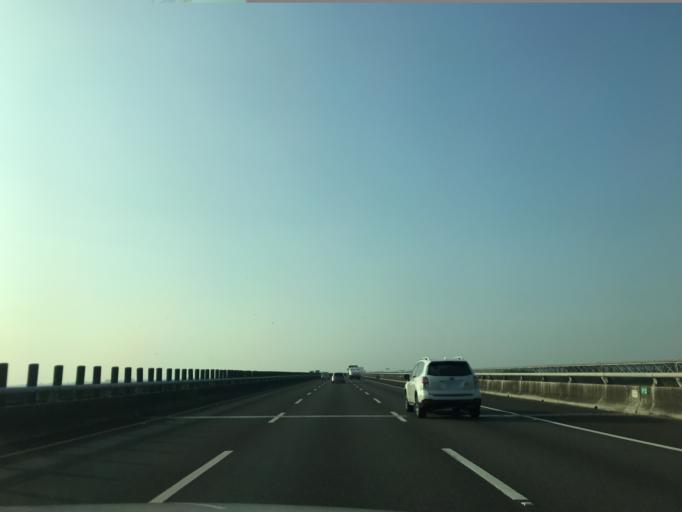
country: TW
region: Taiwan
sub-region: Yunlin
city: Douliu
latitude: 23.8157
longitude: 120.4850
